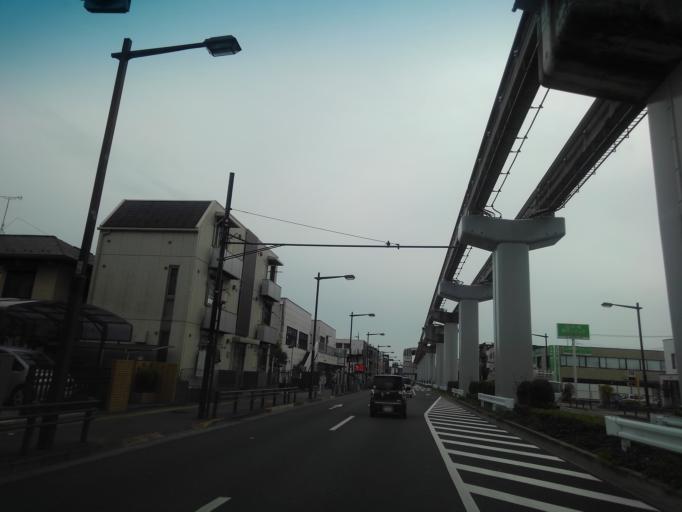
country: JP
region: Tokyo
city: Hino
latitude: 35.7263
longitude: 139.4182
